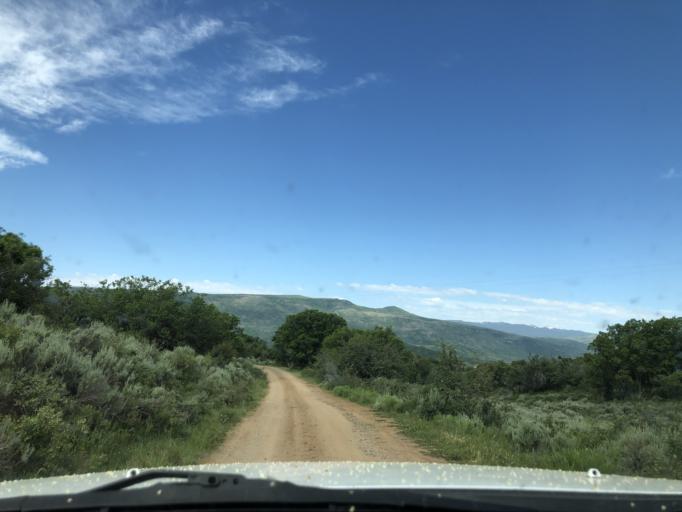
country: US
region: Colorado
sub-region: Delta County
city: Paonia
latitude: 39.0308
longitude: -107.3427
